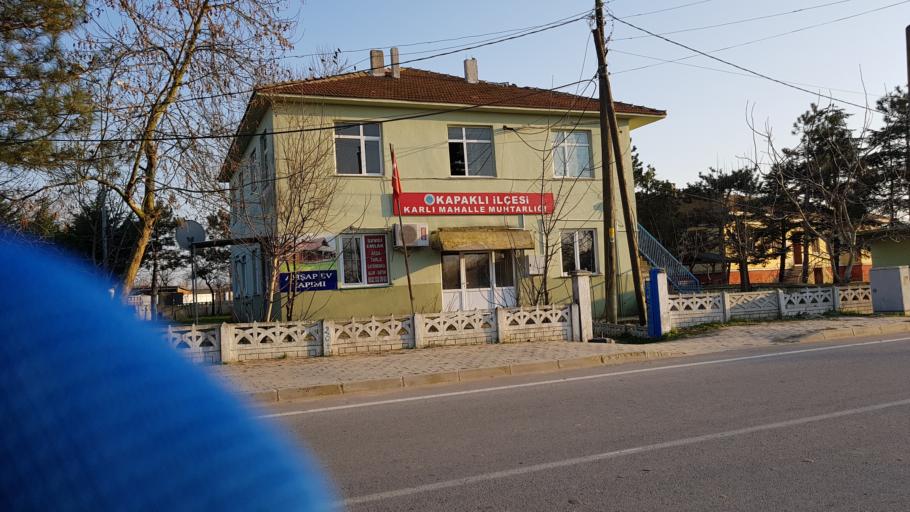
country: TR
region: Tekirdag
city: Saray
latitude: 41.3697
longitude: 27.8656
